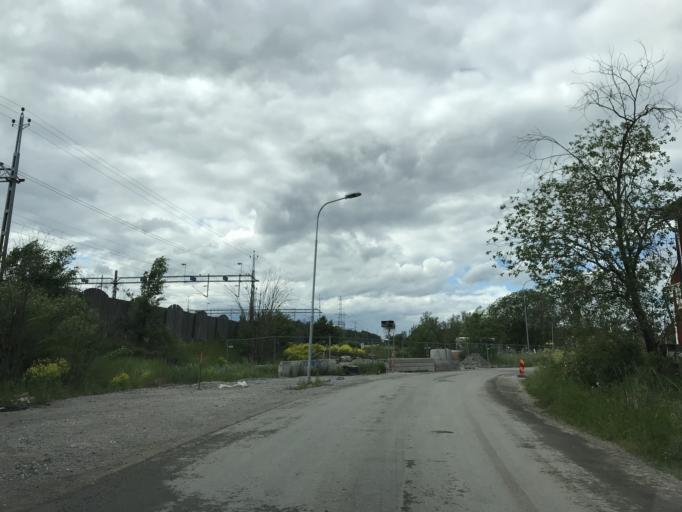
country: SE
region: Stockholm
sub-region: Solna Kommun
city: Rasunda
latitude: 59.3835
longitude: 17.9985
